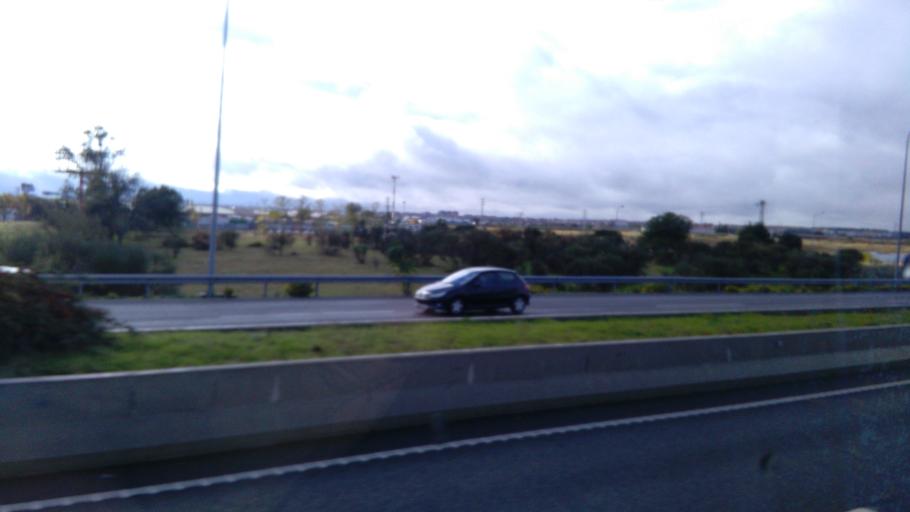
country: ES
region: Madrid
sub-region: Provincia de Madrid
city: Carabanchel
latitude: 40.3648
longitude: -3.7227
